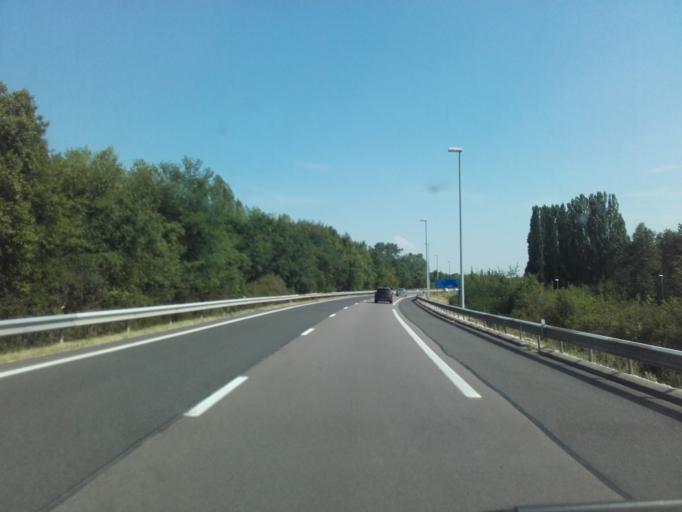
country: FR
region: Bourgogne
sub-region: Departement de la Cote-d'Or
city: Beaune
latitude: 47.0318
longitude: 4.8687
